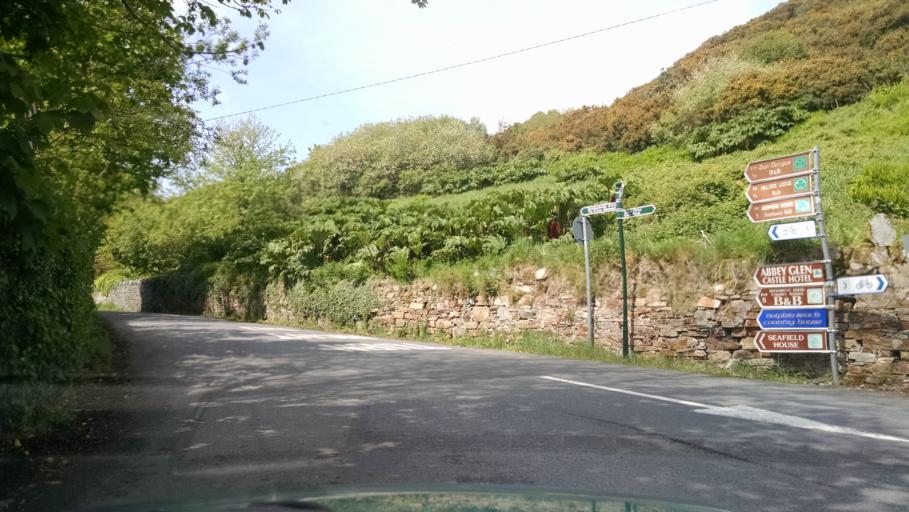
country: IE
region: Connaught
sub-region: County Galway
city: Clifden
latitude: 53.4889
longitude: -10.0270
